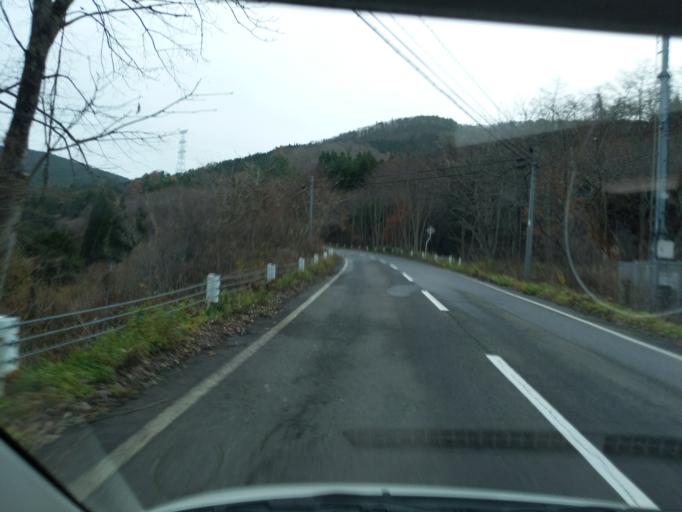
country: JP
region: Iwate
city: Tono
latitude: 39.1769
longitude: 141.3645
